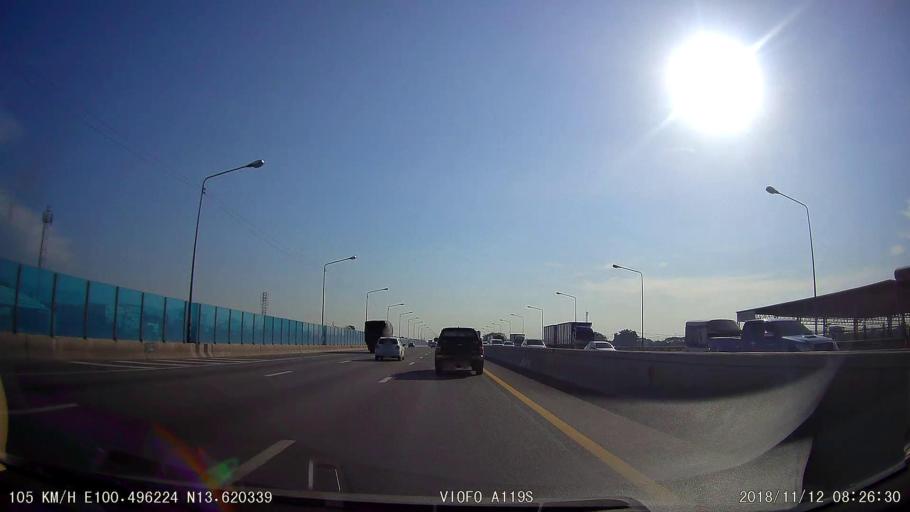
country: TH
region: Bangkok
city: Thung Khru
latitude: 13.6204
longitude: 100.4967
